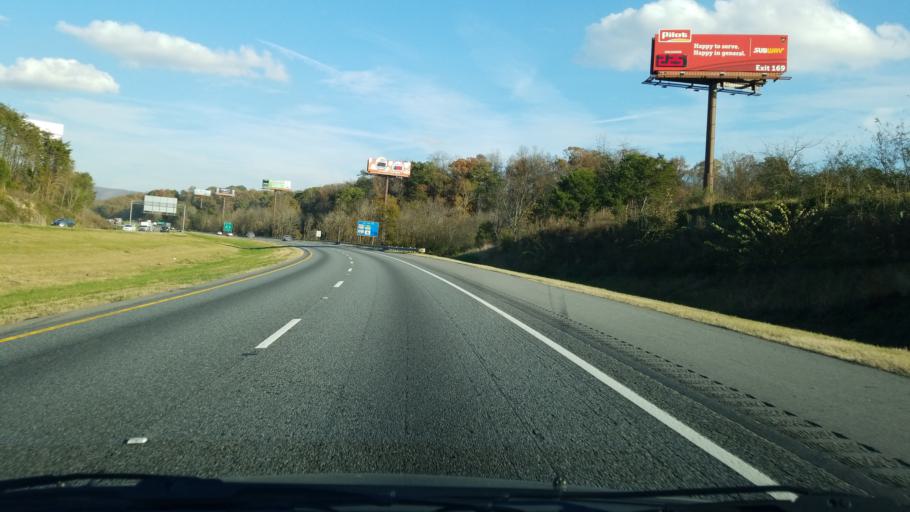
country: US
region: Georgia
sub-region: Walker County
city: Lookout Mountain
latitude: 34.9675
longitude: -85.4355
